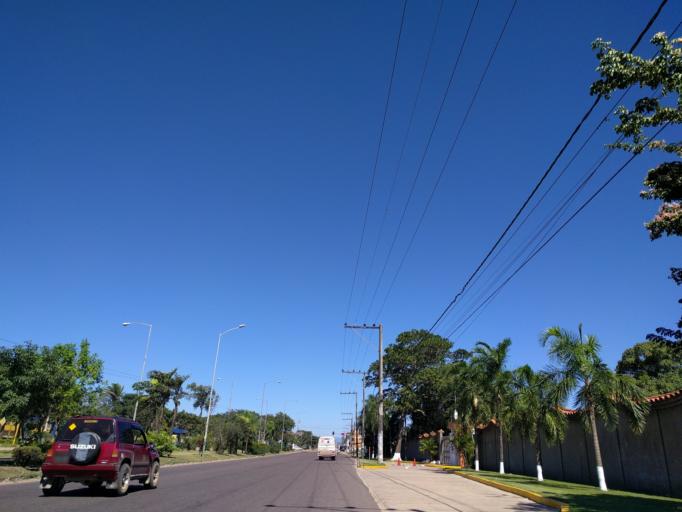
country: BO
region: Santa Cruz
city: Santa Cruz de la Sierra
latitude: -17.8365
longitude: -63.2362
